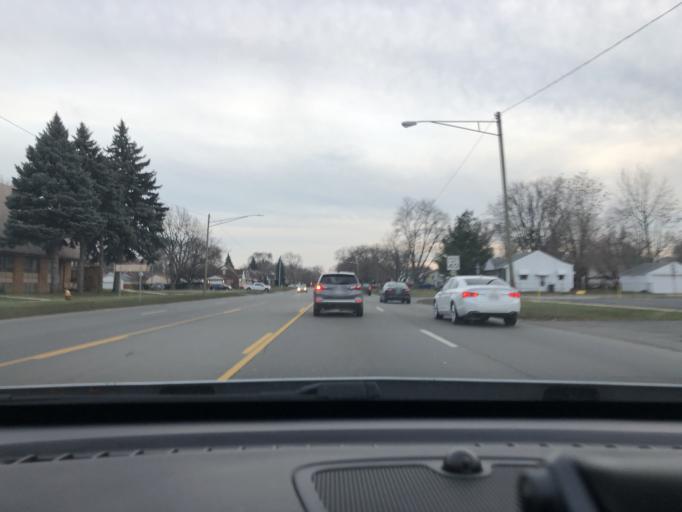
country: US
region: Michigan
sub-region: Wayne County
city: Allen Park
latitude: 42.2552
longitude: -83.2312
